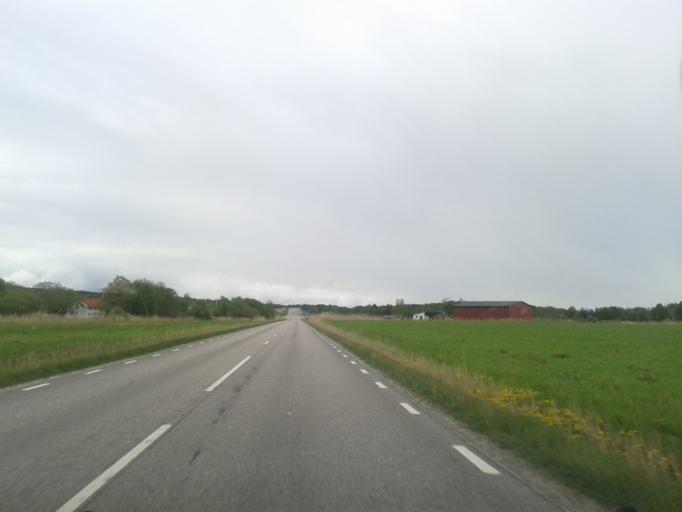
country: SE
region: Vaestra Goetaland
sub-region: Stenungsunds Kommun
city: Stora Hoga
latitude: 57.9795
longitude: 11.8262
